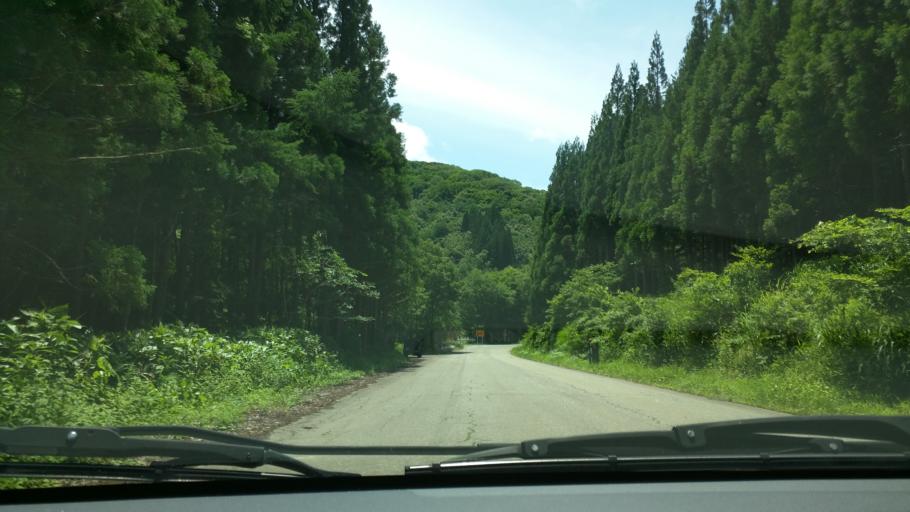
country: JP
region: Tochigi
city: Kuroiso
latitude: 37.2547
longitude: 139.7729
